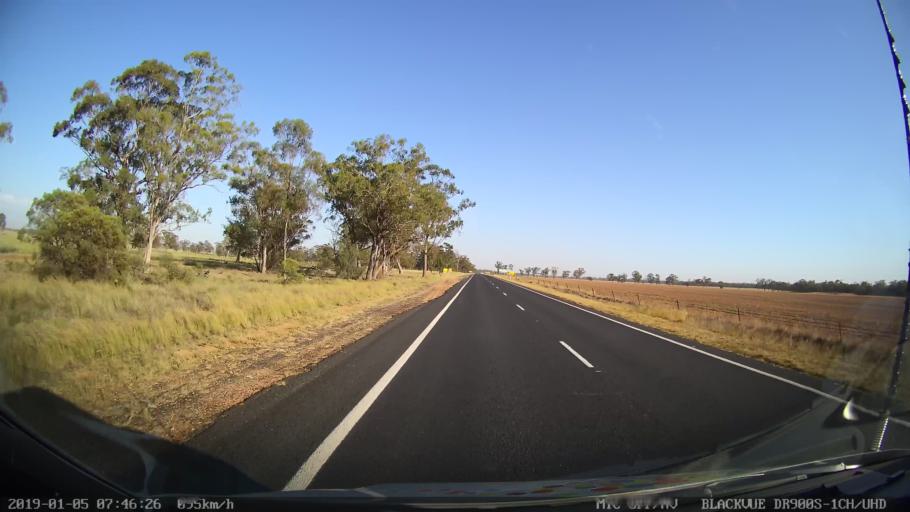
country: AU
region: New South Wales
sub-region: Gilgandra
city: Gilgandra
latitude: -31.8445
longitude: 148.6434
